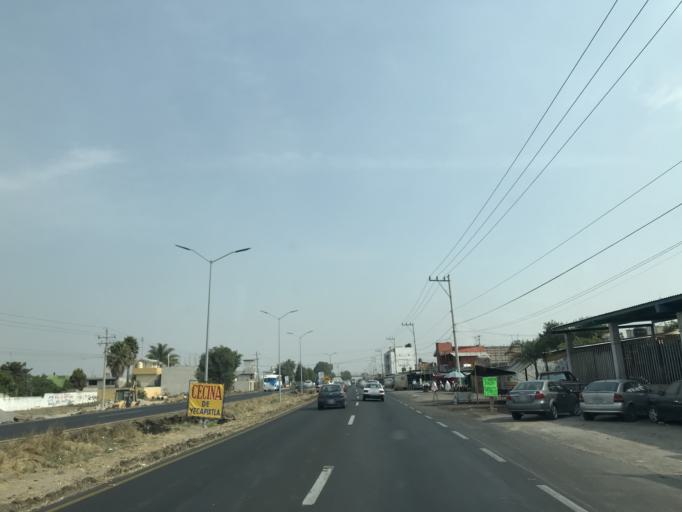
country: MX
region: Tlaxcala
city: Tenancingo
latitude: 19.1435
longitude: -98.1915
